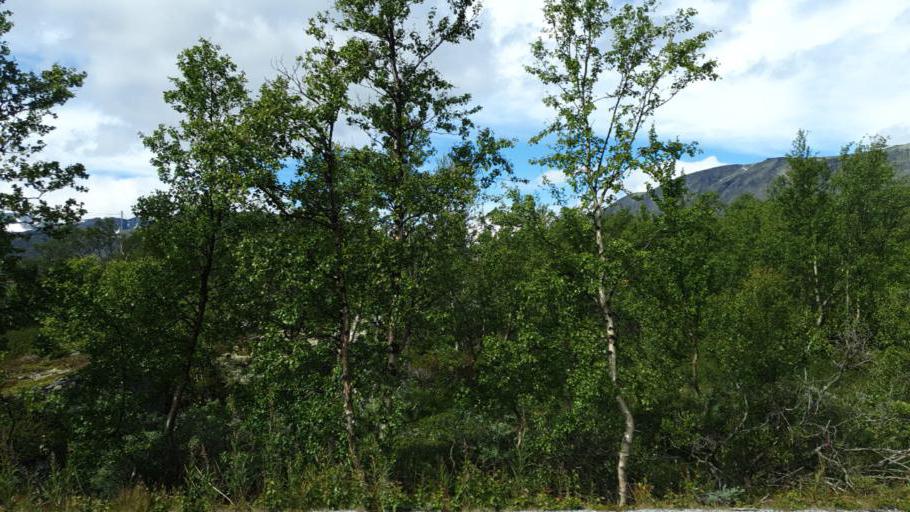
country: NO
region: Oppland
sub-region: Oystre Slidre
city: Heggenes
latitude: 61.4889
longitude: 8.8393
